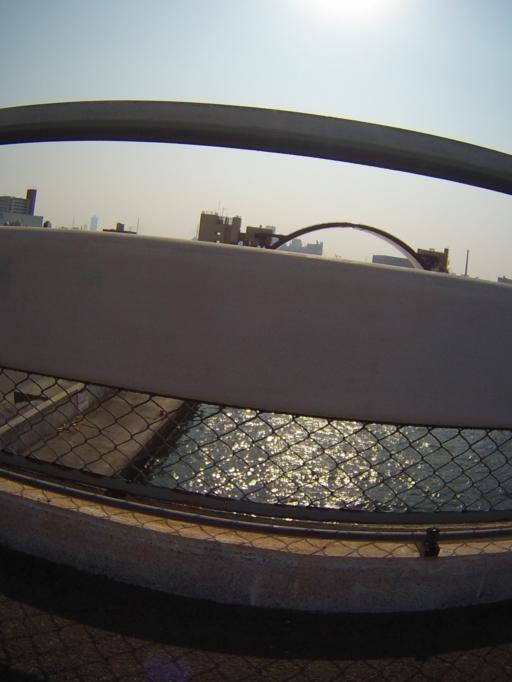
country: JP
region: Osaka
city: Osaka-shi
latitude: 34.6762
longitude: 135.4578
